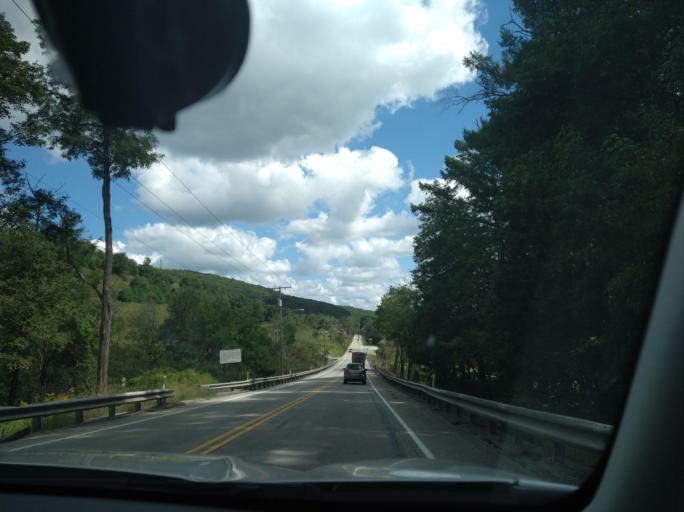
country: US
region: Pennsylvania
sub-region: Westmoreland County
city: Ligonier
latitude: 40.0667
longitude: -79.2492
